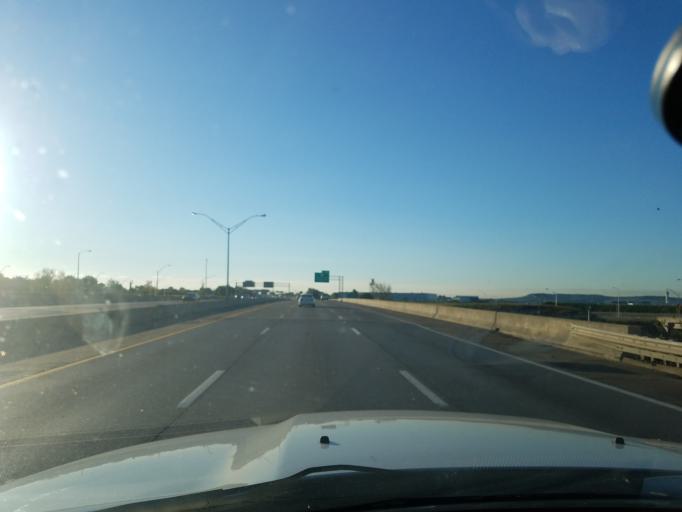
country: US
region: Kentucky
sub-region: Jefferson County
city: Audubon Park
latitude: 38.1911
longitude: -85.7301
